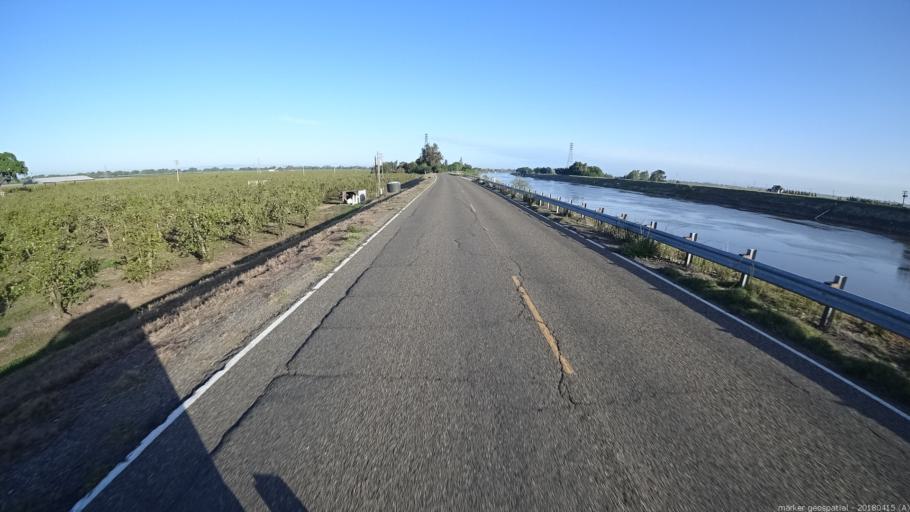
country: US
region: California
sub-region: Sacramento County
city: Walnut Grove
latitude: 38.2888
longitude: -121.5593
